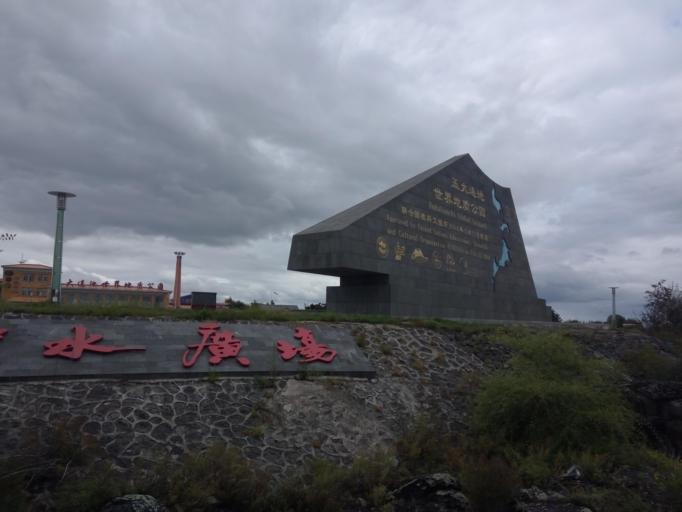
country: CN
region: Heilongjiang Sheng
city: Erjing
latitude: 48.6506
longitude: 126.1521
